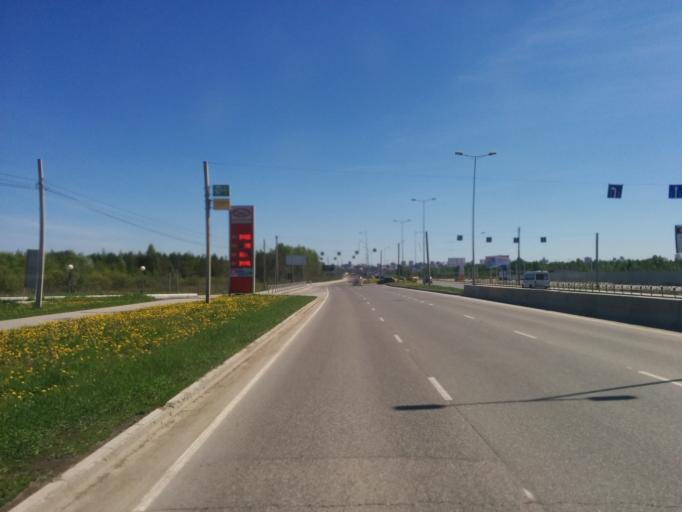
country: RU
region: Perm
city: Perm
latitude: 58.0348
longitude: 56.2015
